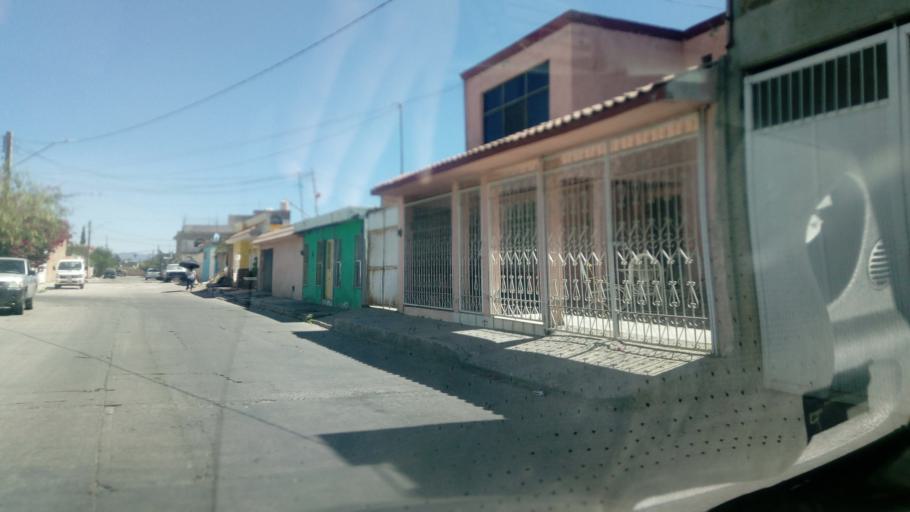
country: MX
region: Durango
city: Victoria de Durango
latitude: 24.0137
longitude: -104.6570
